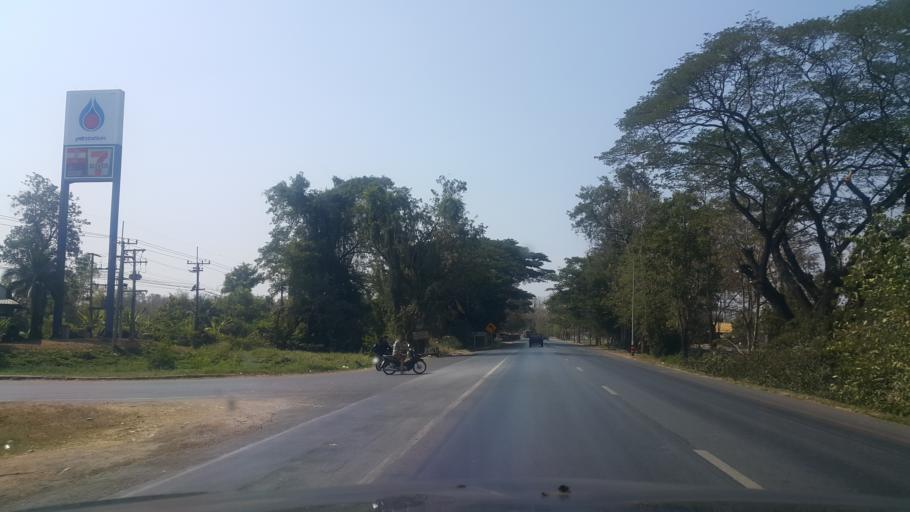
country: TH
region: Nakhon Ratchasima
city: Pak Thong Chai
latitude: 14.5699
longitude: 101.9815
